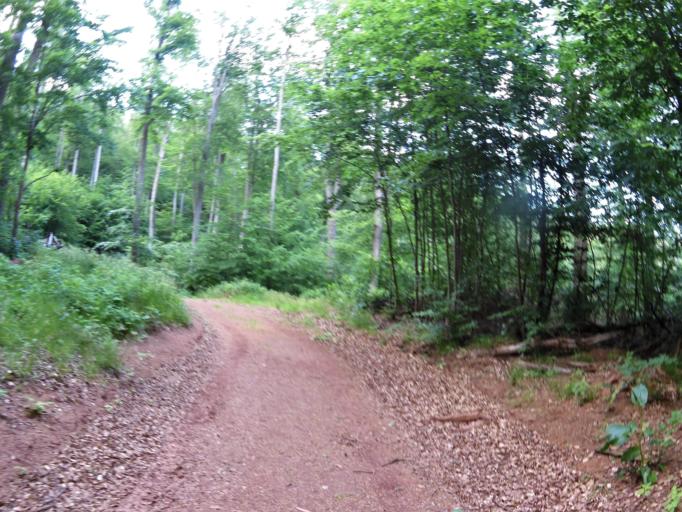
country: DE
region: Thuringia
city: Wolfsburg-Unkeroda
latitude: 50.9242
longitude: 10.3053
